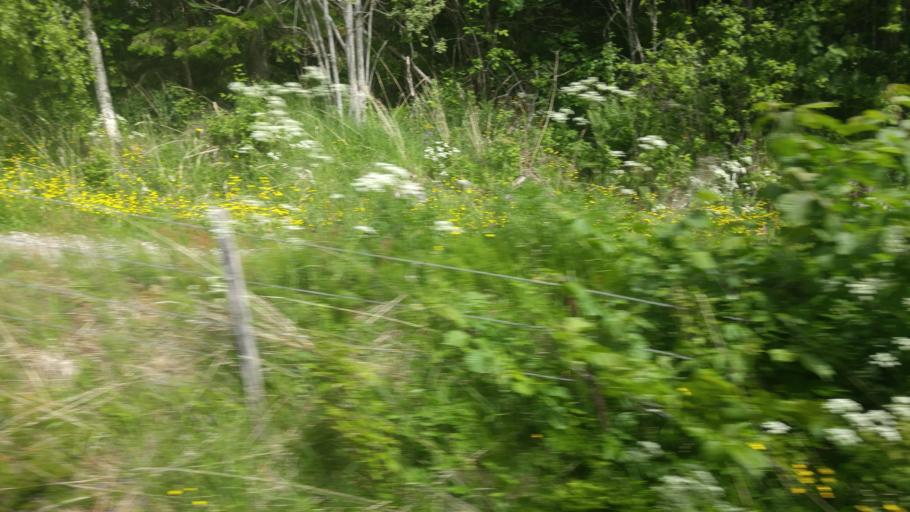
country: NO
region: Sor-Trondelag
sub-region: Midtre Gauldal
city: Storen
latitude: 63.0197
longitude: 10.4176
